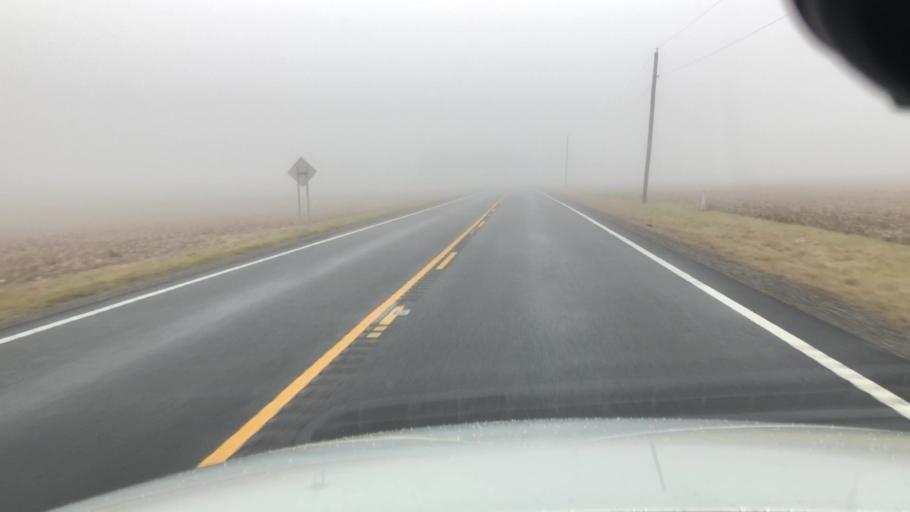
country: US
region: Ohio
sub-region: Logan County
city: Russells Point
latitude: 40.5660
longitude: -83.8436
